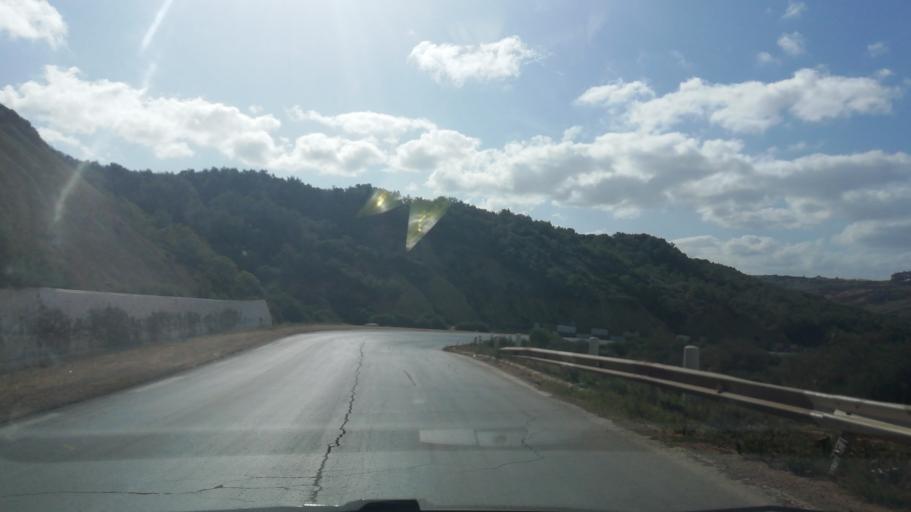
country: DZ
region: Relizane
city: Mazouna
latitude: 36.3225
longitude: 0.6855
